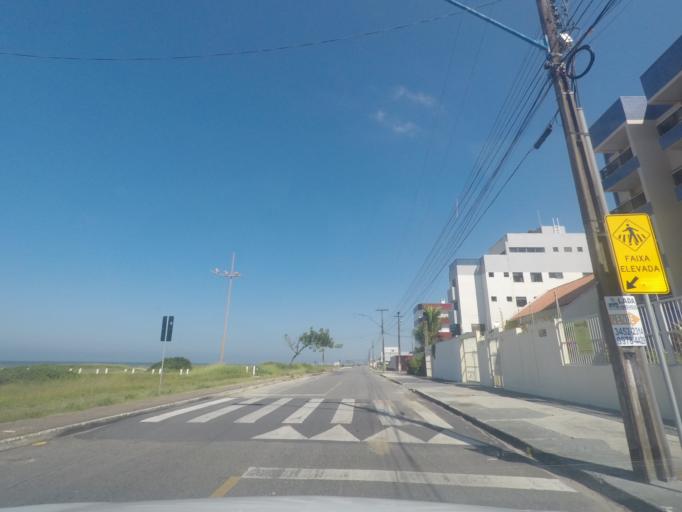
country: BR
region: Parana
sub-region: Pontal Do Parana
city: Pontal do Parana
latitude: -25.7406
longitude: -48.4947
